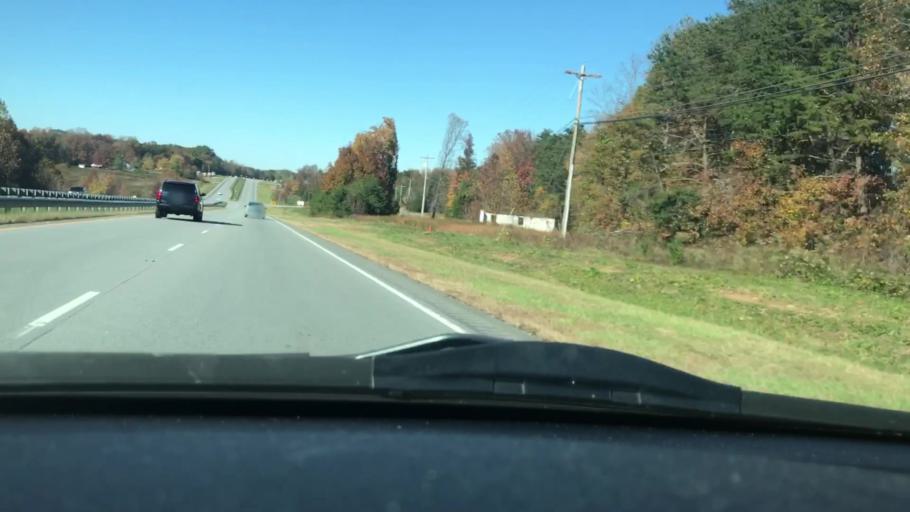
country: US
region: North Carolina
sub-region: Rockingham County
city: Madison
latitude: 36.3177
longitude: -79.9437
